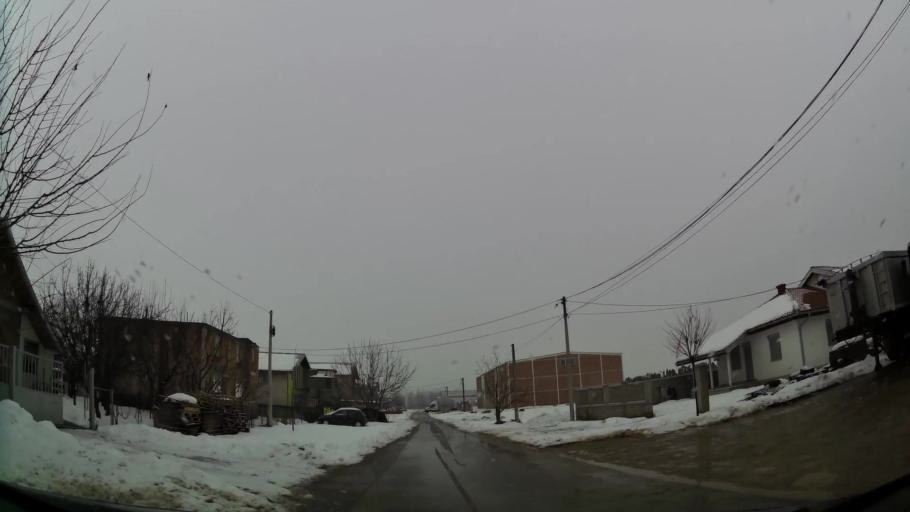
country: RS
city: Novi Banovci
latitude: 44.8790
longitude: 20.3180
